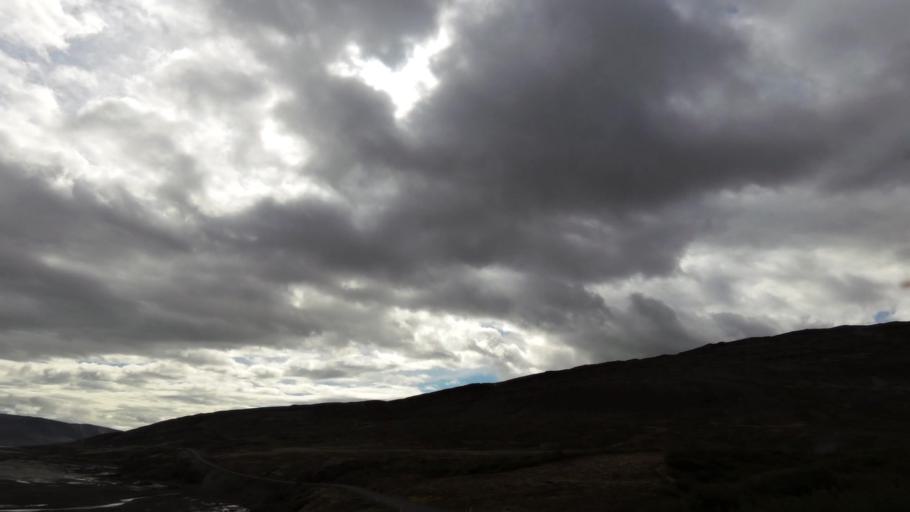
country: IS
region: West
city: Stykkisholmur
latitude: 65.5902
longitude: -22.1456
